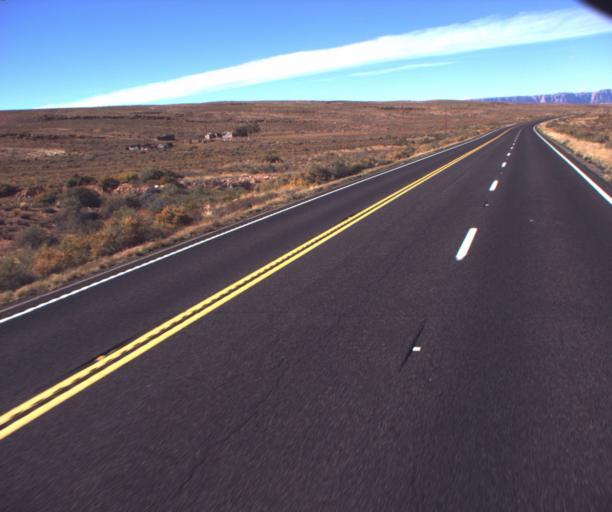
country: US
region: Arizona
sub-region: Coconino County
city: LeChee
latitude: 36.5580
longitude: -111.6328
